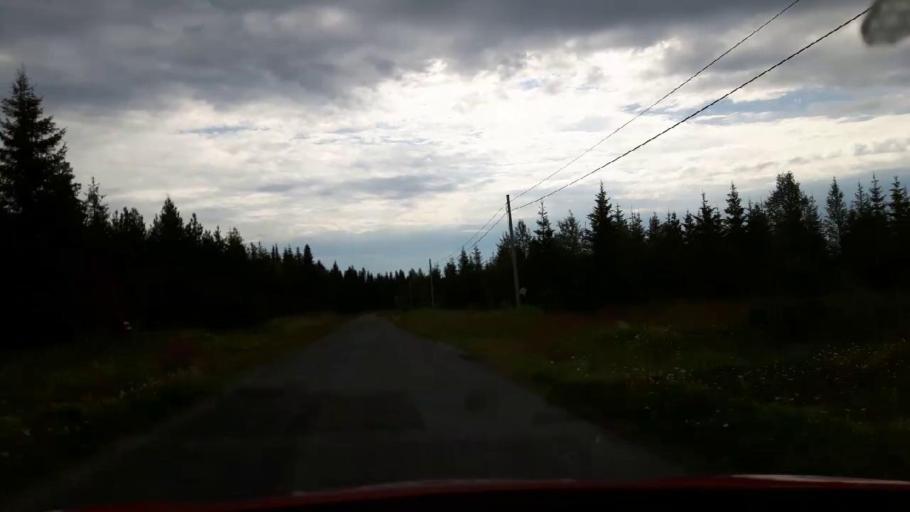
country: SE
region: Jaemtland
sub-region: OEstersunds Kommun
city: Lit
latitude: 63.3703
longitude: 15.1324
